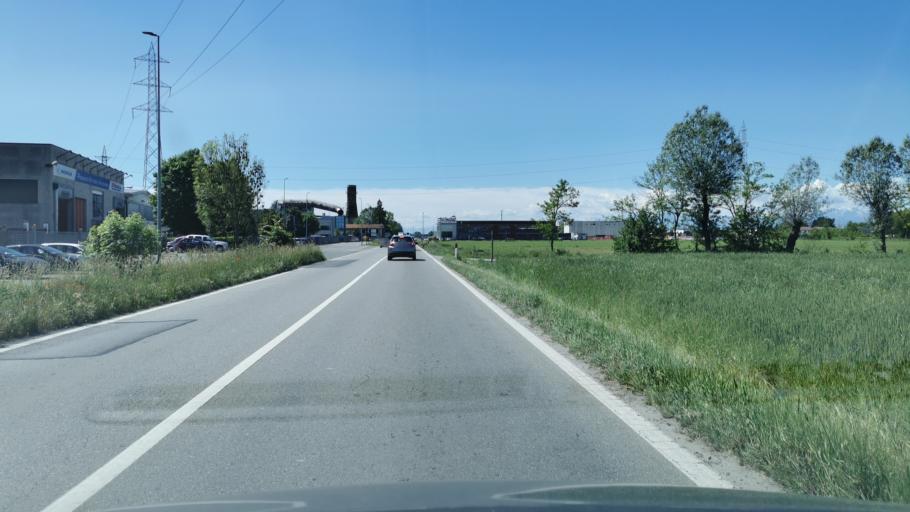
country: IT
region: Piedmont
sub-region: Provincia di Torino
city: Settimo Torinese
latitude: 45.1503
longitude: 7.7472
